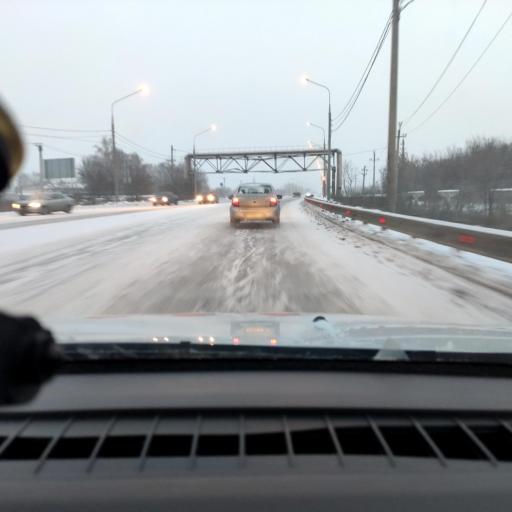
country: RU
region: Samara
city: Otradnyy
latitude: 53.3733
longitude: 51.3709
